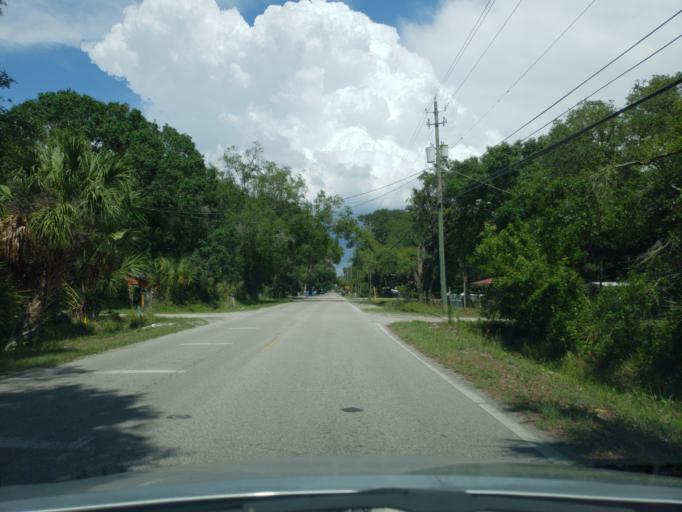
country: US
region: Florida
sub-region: Hillsborough County
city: Palm River-Clair Mel
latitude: 27.9335
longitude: -82.3881
